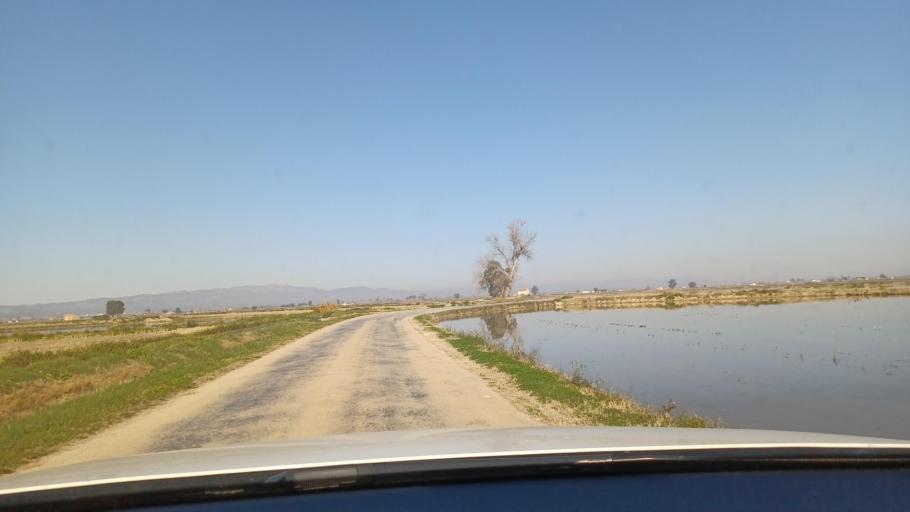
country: ES
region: Catalonia
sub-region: Provincia de Tarragona
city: Deltebre
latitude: 40.6909
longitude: 0.6514
